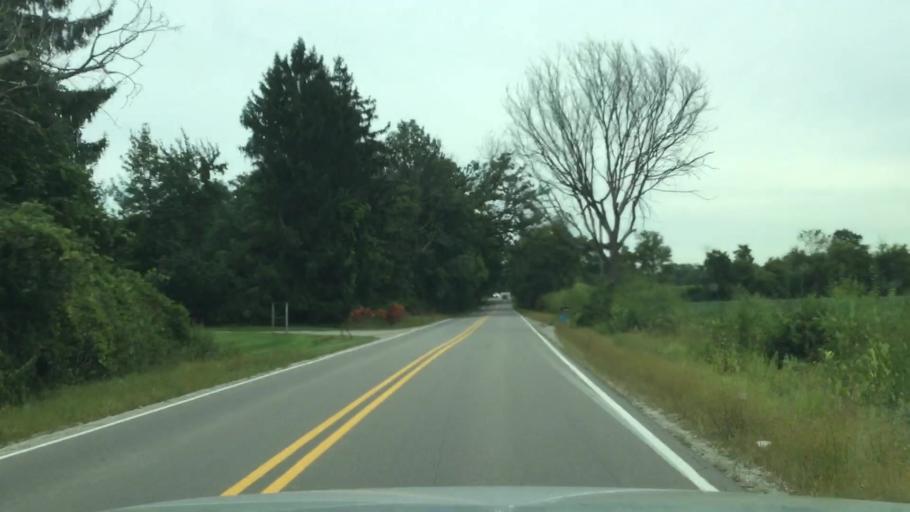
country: US
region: Michigan
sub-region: Washtenaw County
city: Ypsilanti
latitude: 42.1952
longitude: -83.6310
